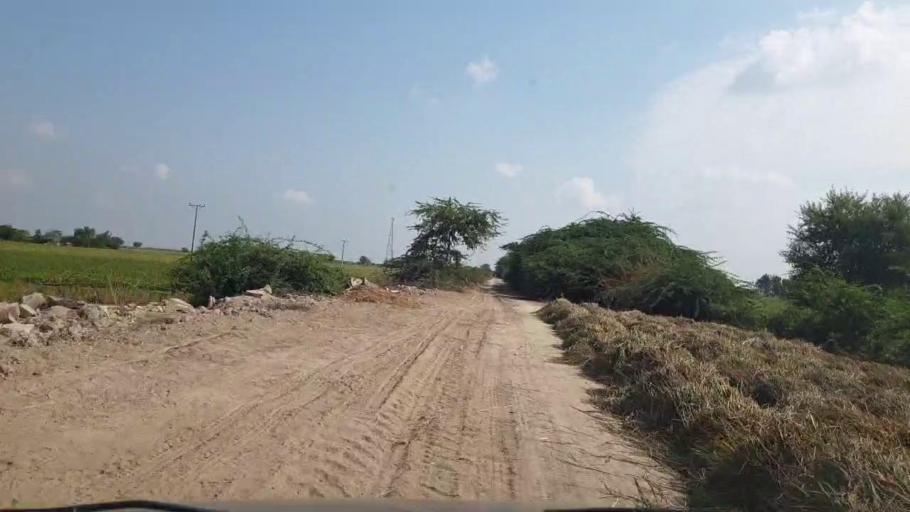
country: PK
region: Sindh
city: Jati
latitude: 24.4658
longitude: 68.5724
